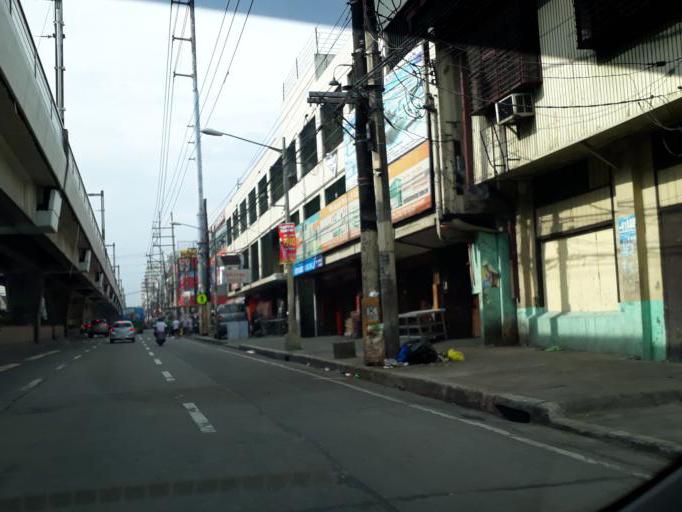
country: PH
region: Calabarzon
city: Del Monte
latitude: 14.6395
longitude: 120.9836
